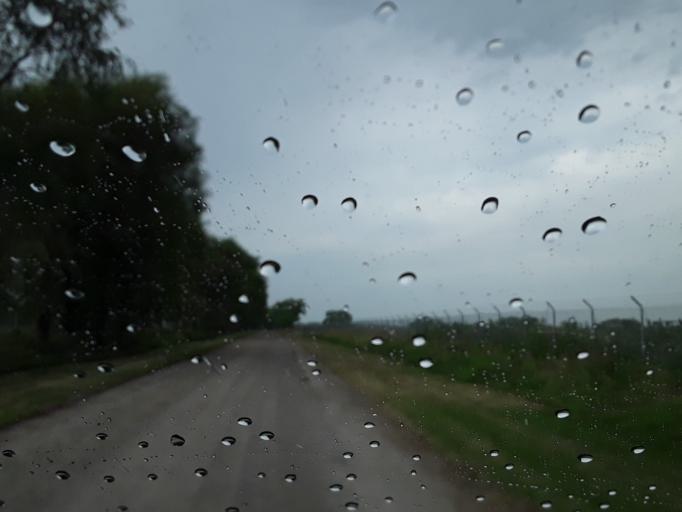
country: US
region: Nebraska
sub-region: Saunders County
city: Yutan
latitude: 41.1879
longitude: -96.4449
